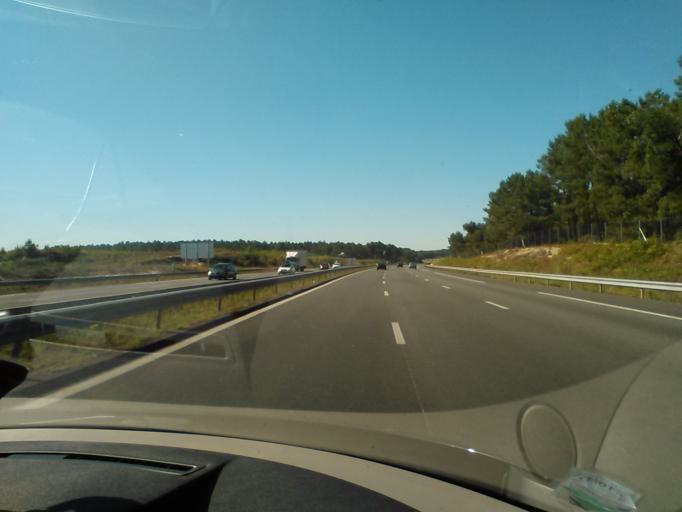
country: FR
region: Aquitaine
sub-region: Departement de la Gironde
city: Salles
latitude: 44.5238
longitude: -0.8378
